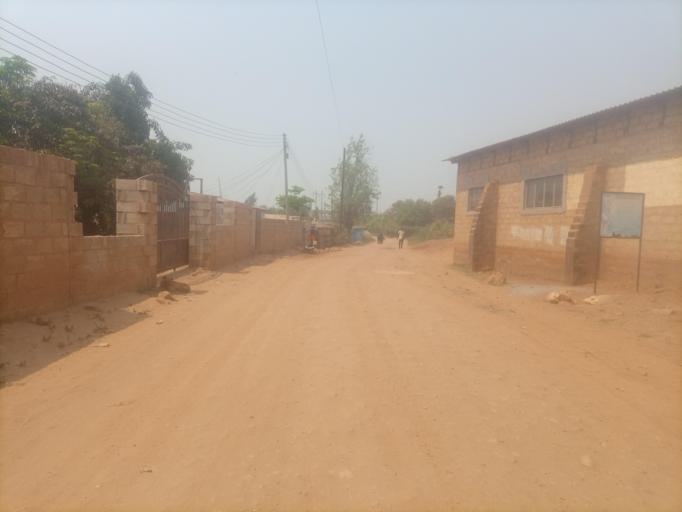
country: ZM
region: Lusaka
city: Lusaka
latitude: -15.3922
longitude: 28.3674
